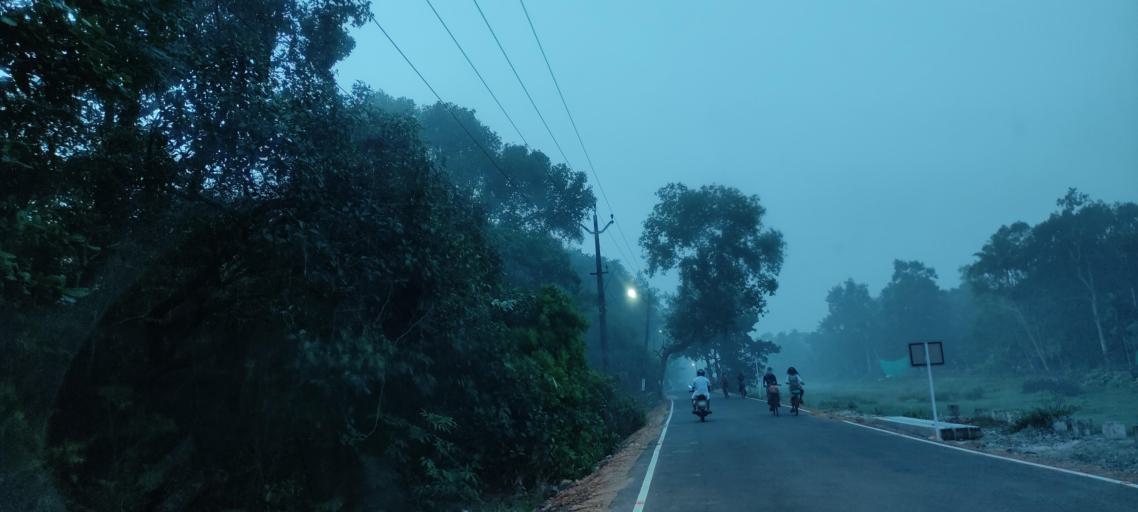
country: IN
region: Kerala
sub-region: Alappuzha
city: Shertallai
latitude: 9.6084
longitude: 76.3339
